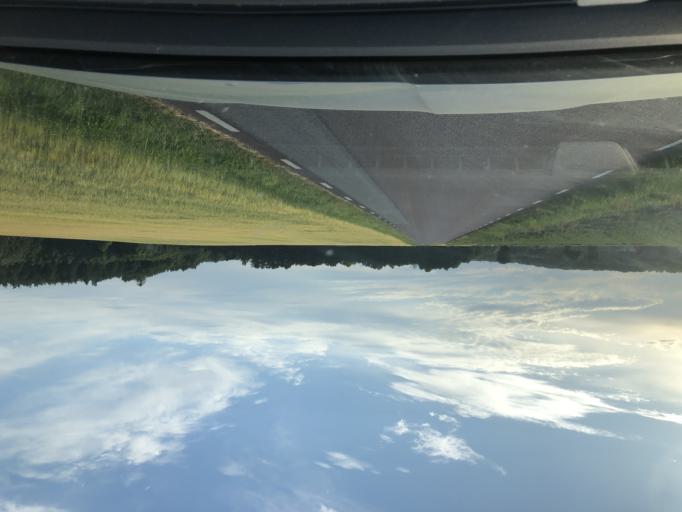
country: SE
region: Blekinge
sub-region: Solvesborgs Kommun
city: Soelvesborg
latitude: 56.1215
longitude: 14.6174
